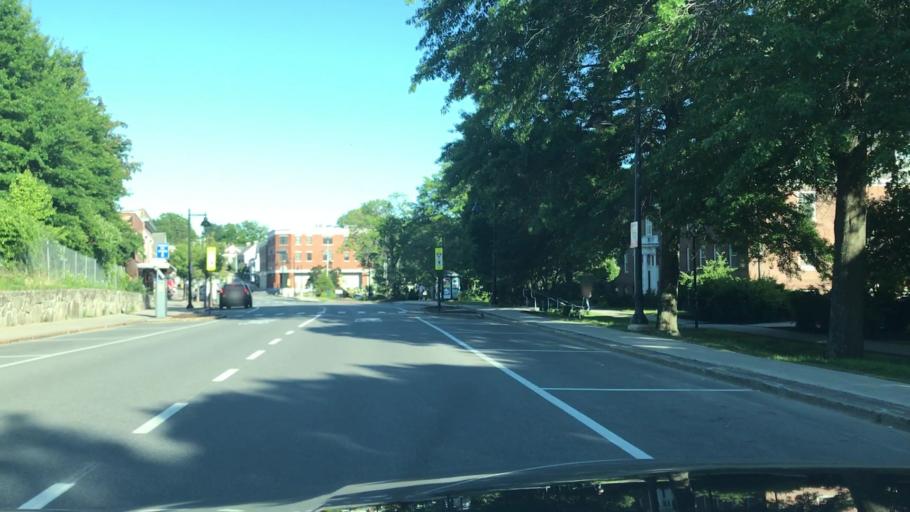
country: US
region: New Hampshire
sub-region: Strafford County
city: Durham
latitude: 43.1348
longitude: -70.9278
